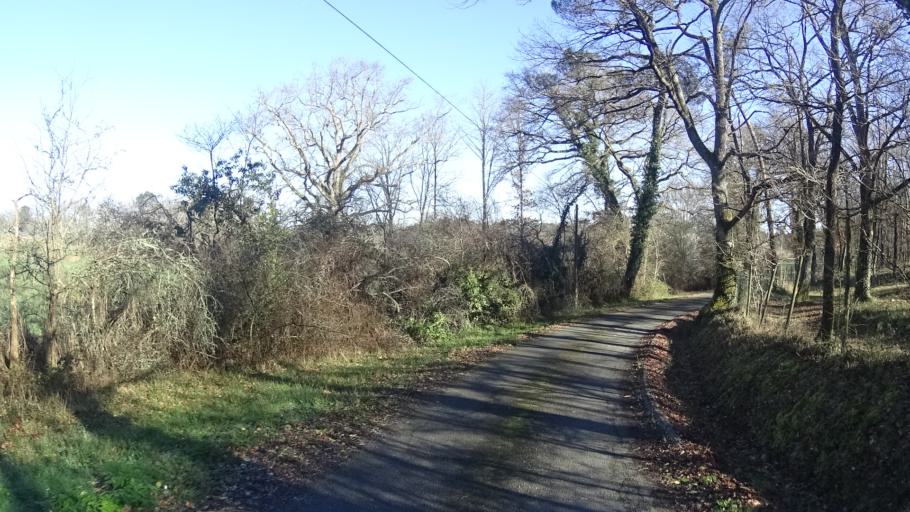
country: FR
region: Aquitaine
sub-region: Departement de la Dordogne
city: La Roche-Chalais
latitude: 45.1568
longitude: 0.0161
